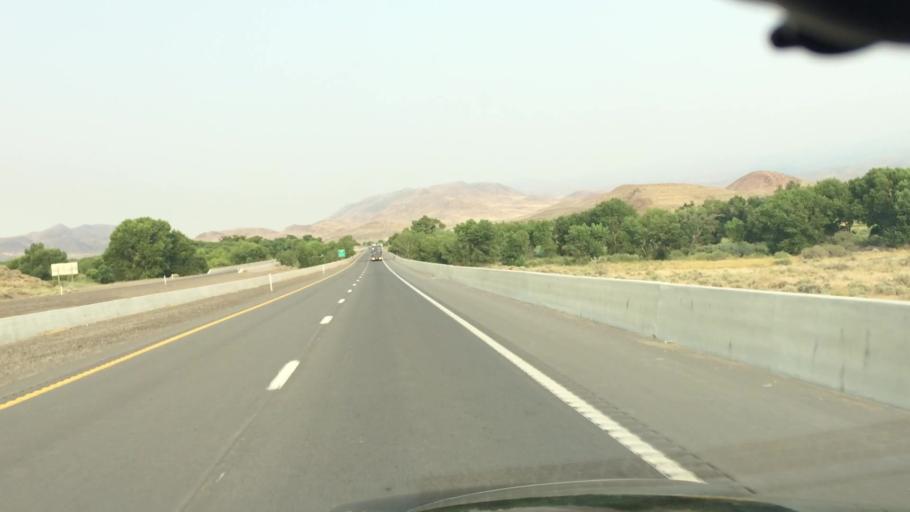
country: US
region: Nevada
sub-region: Lyon County
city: Fernley
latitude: 39.6182
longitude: -119.2909
